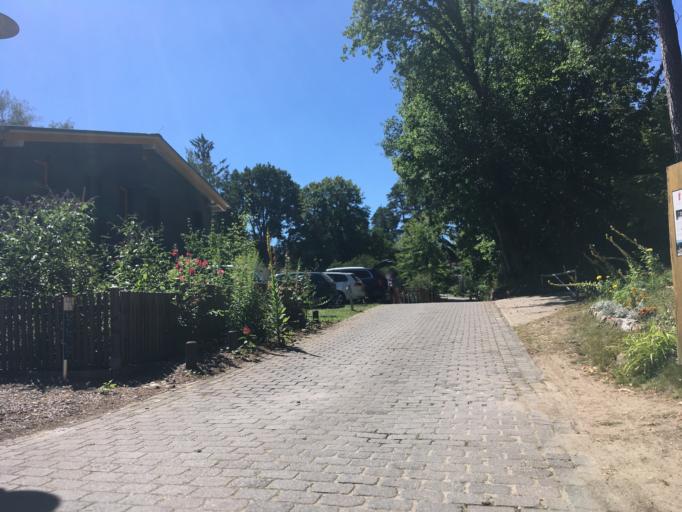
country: DE
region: Brandenburg
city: Grosswoltersdorf
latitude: 53.1477
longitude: 13.0458
